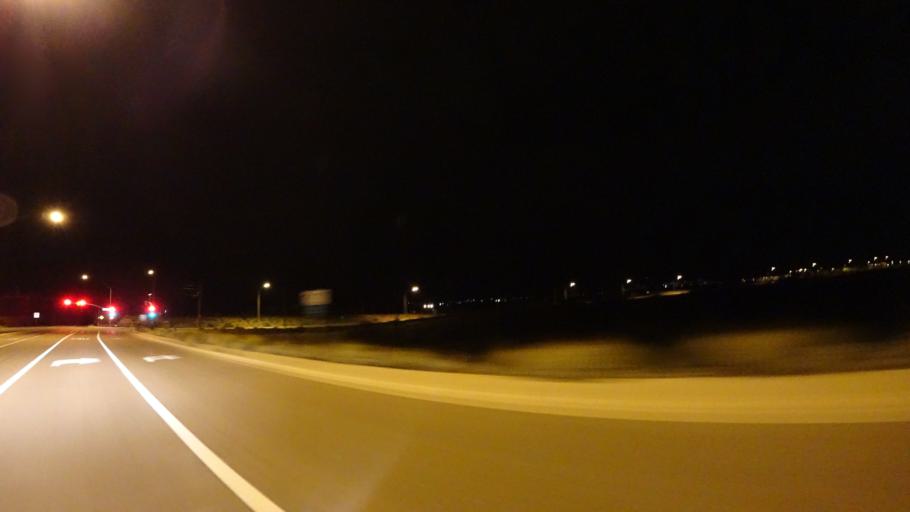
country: US
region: Arizona
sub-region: Maricopa County
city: Mesa
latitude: 33.4830
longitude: -111.7185
